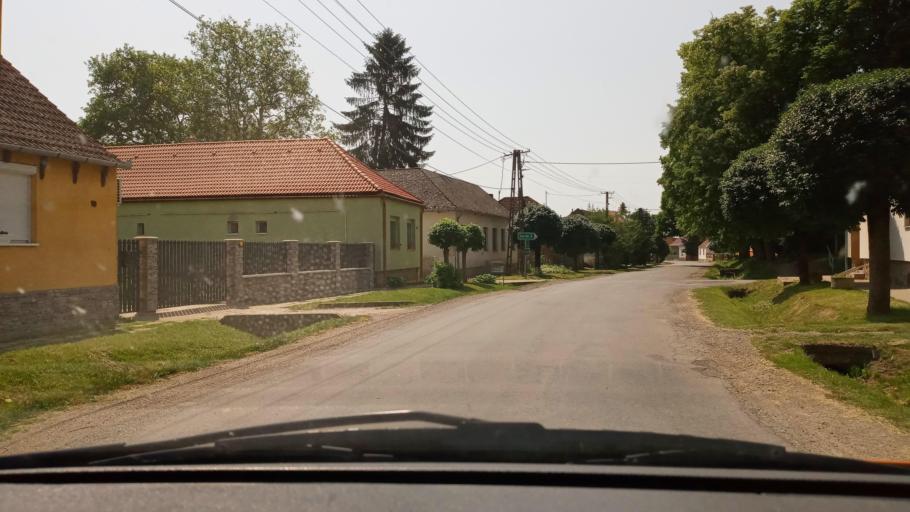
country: HU
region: Baranya
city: Szentlorinc
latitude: 46.0085
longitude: 18.0424
